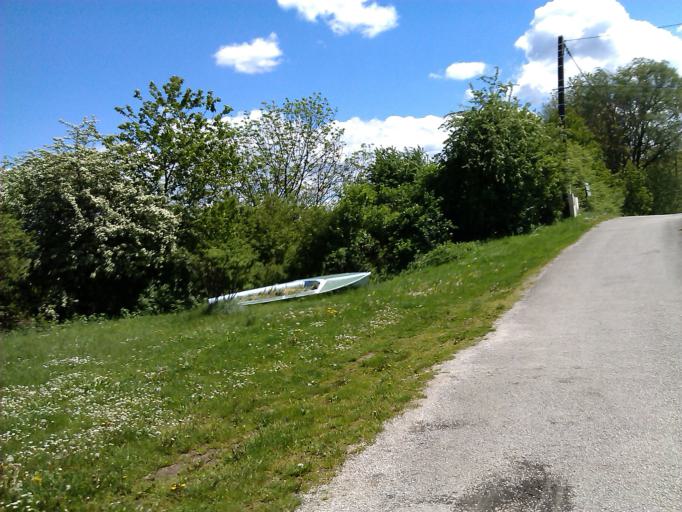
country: FR
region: Franche-Comte
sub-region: Departement du Doubs
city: Etupes
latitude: 47.5228
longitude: 6.8811
